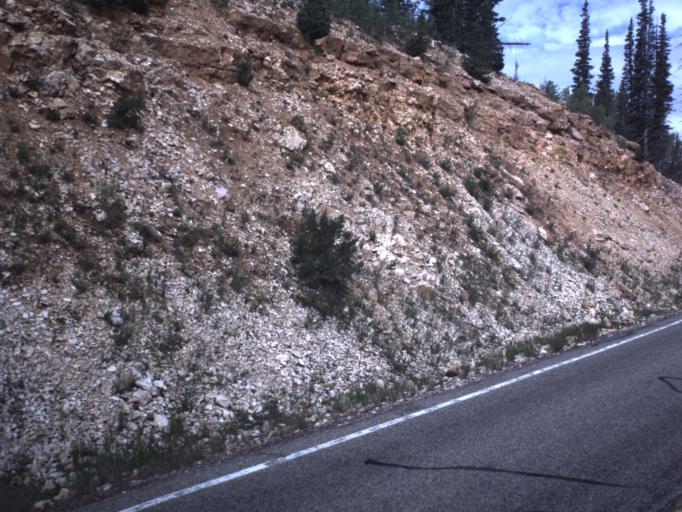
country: US
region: Utah
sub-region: Iron County
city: Parowan
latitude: 37.5382
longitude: -112.7746
